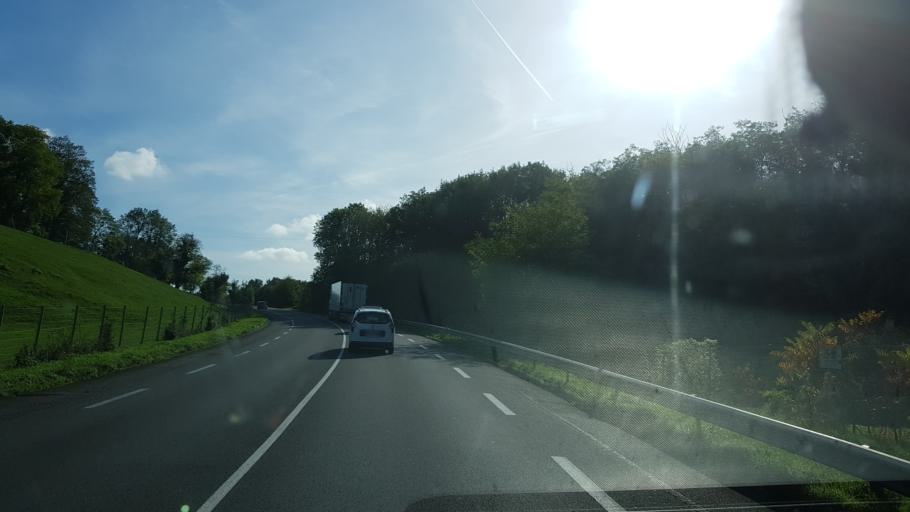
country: FR
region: Poitou-Charentes
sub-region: Departement de la Charente
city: Saint-Claud
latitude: 45.8863
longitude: 0.4693
